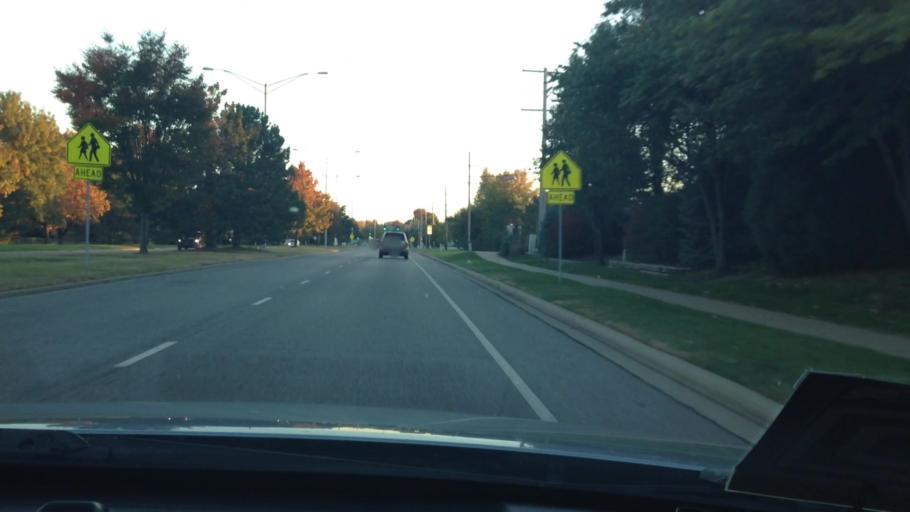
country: US
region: Kansas
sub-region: Johnson County
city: Lenexa
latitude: 38.9062
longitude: -94.7053
